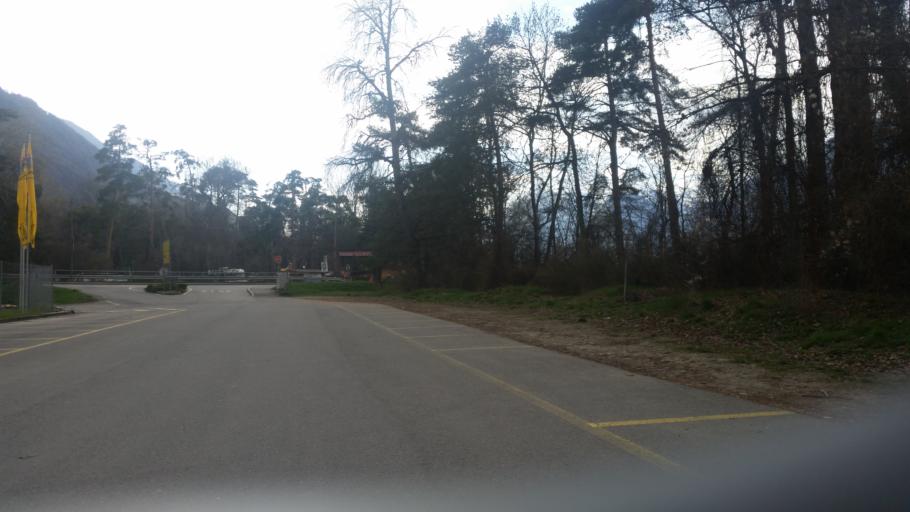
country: CH
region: Valais
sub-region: Conthey District
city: Conthey
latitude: 46.2118
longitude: 7.3132
